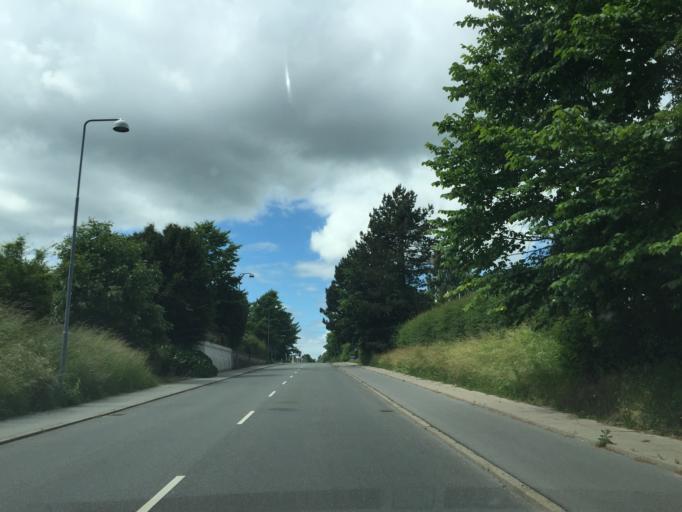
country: DK
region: South Denmark
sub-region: Svendborg Kommune
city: Svendborg
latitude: 55.0678
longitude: 10.5780
